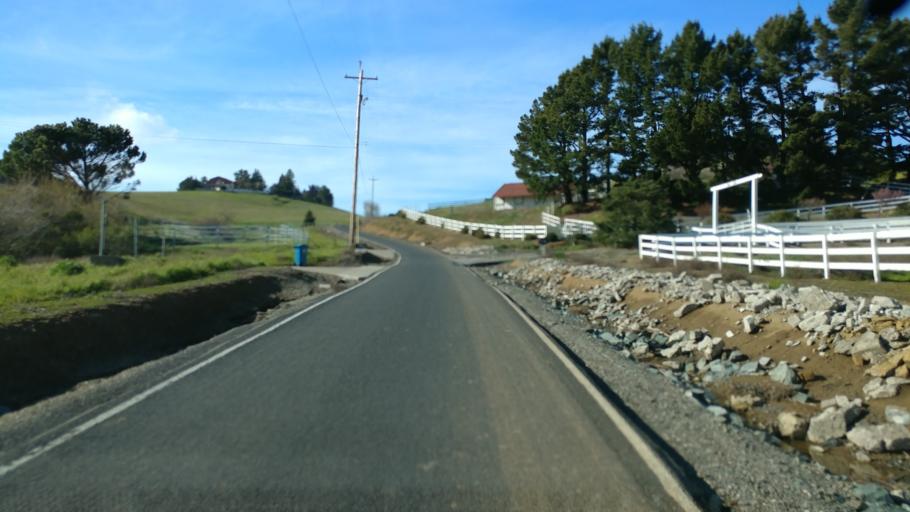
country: US
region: California
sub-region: Alameda County
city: Livermore
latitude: 37.7980
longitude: -121.7809
